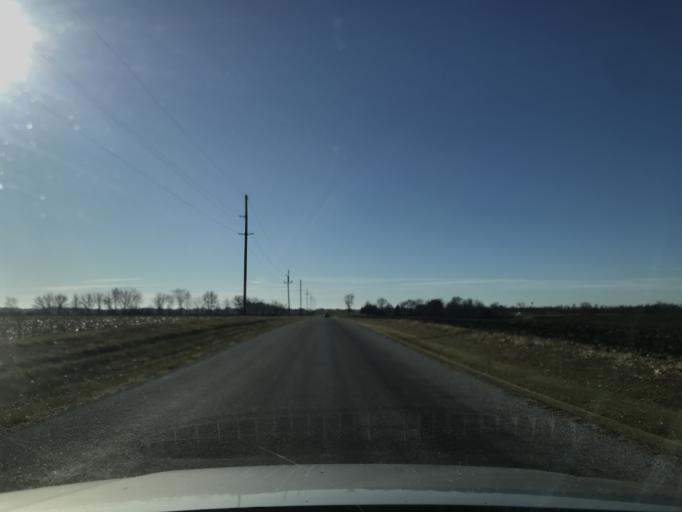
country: US
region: Illinois
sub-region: Hancock County
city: Carthage
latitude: 40.4665
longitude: -91.1783
